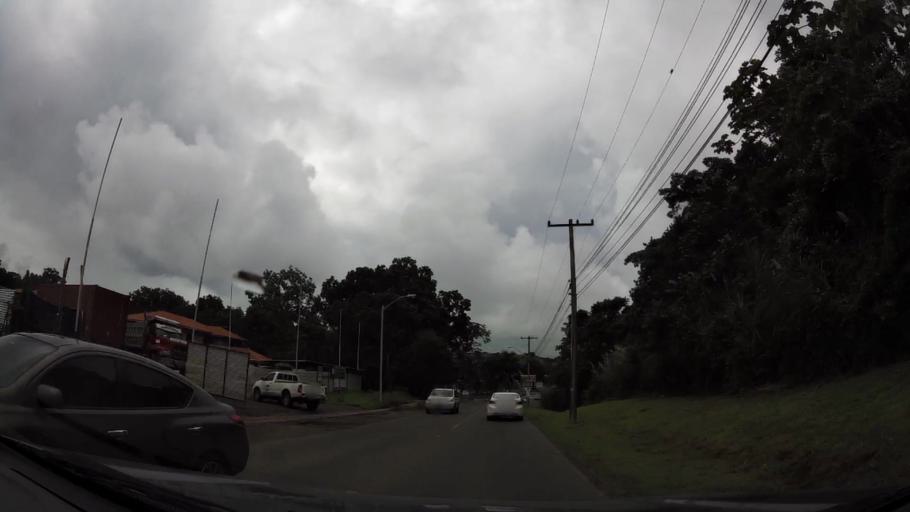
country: PA
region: Panama
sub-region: Distrito de Panama
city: Ancon
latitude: 8.9942
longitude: -79.5571
